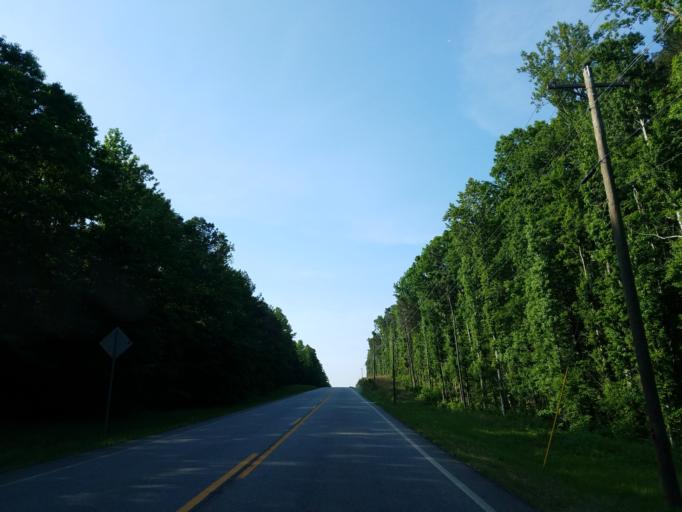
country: US
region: Georgia
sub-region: Whitfield County
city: Dalton
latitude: 34.6594
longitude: -85.0593
